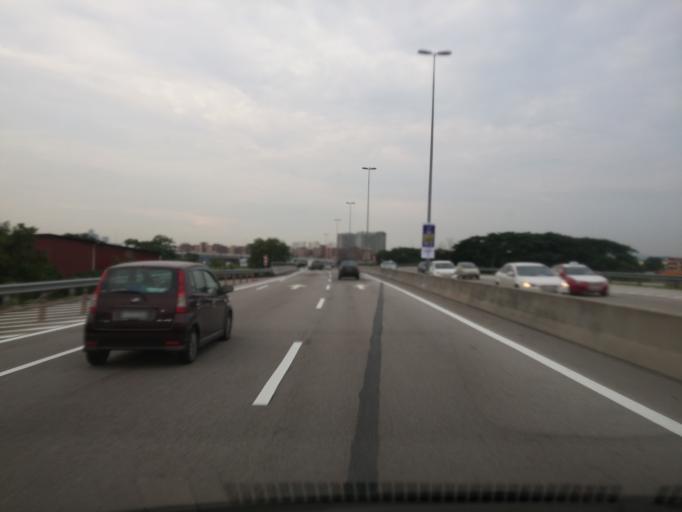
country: MY
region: Kuala Lumpur
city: Kuala Lumpur
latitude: 3.1150
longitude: 101.7154
